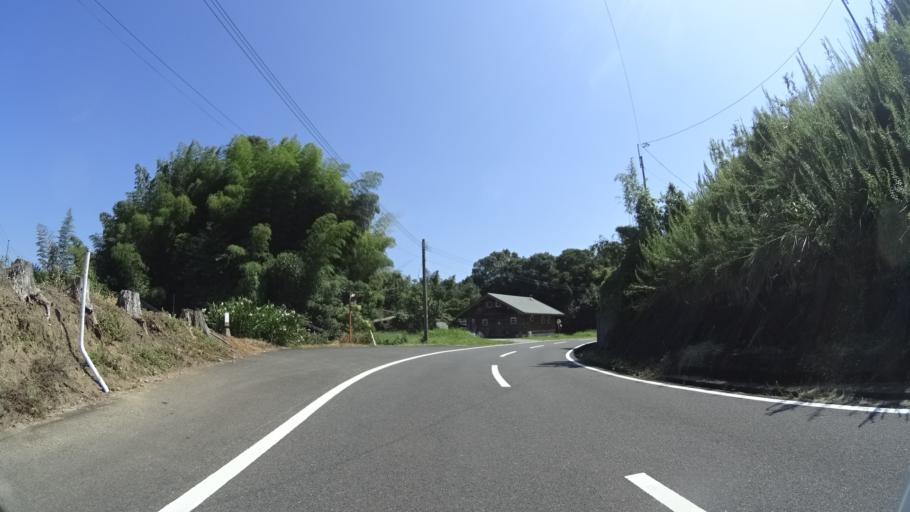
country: JP
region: Kagoshima
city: Kajiki
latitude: 31.7605
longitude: 130.6709
